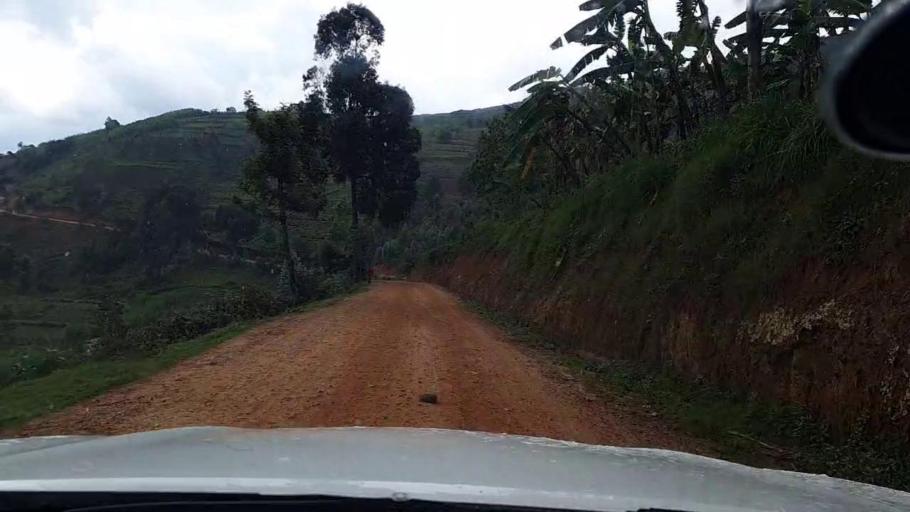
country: RW
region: Western Province
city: Kibuye
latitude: -2.1522
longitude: 29.4284
